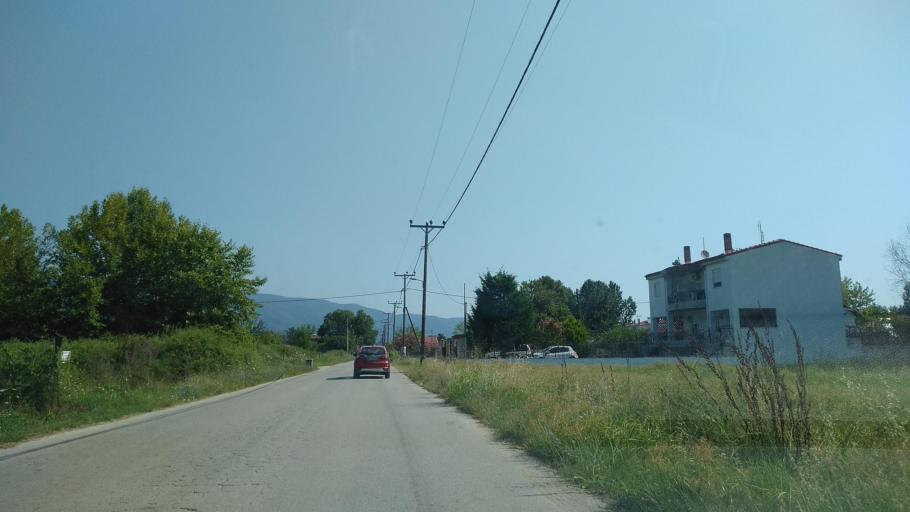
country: GR
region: Central Macedonia
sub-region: Nomos Thessalonikis
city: Stavros
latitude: 40.6823
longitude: 23.6875
